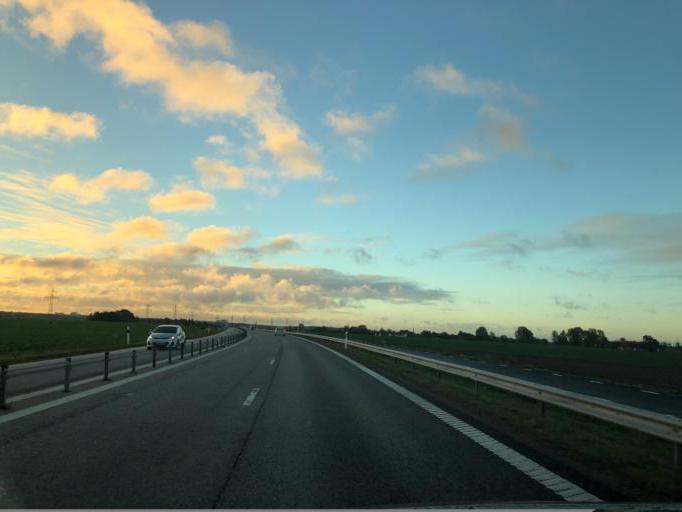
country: SE
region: Skane
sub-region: Kavlinge Kommun
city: Kaevlinge
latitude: 55.7541
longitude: 13.1313
